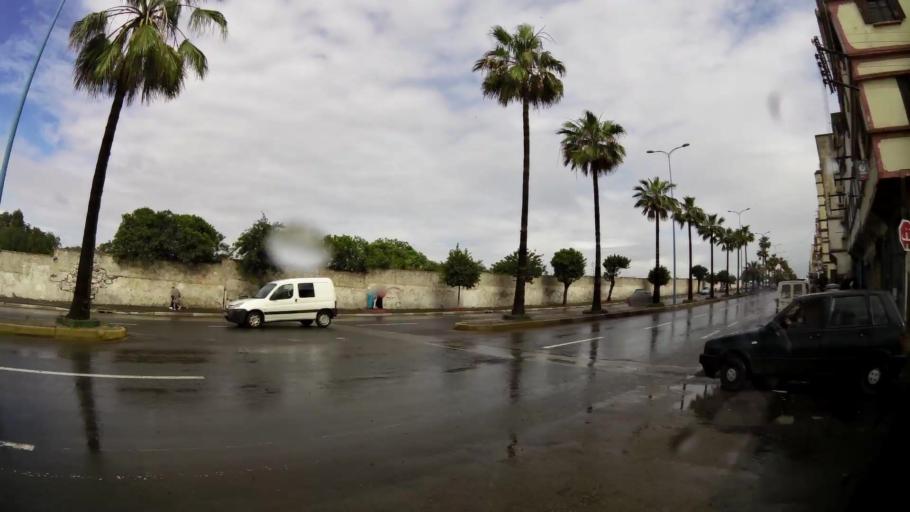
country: MA
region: Grand Casablanca
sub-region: Casablanca
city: Casablanca
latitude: 33.5484
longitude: -7.5662
